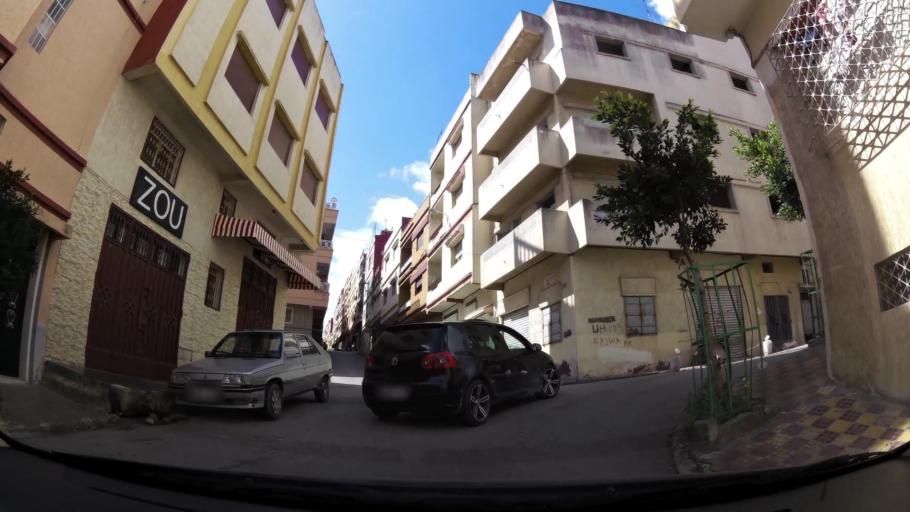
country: MA
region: Tanger-Tetouan
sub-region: Tanger-Assilah
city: Tangier
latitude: 35.7761
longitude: -5.8277
